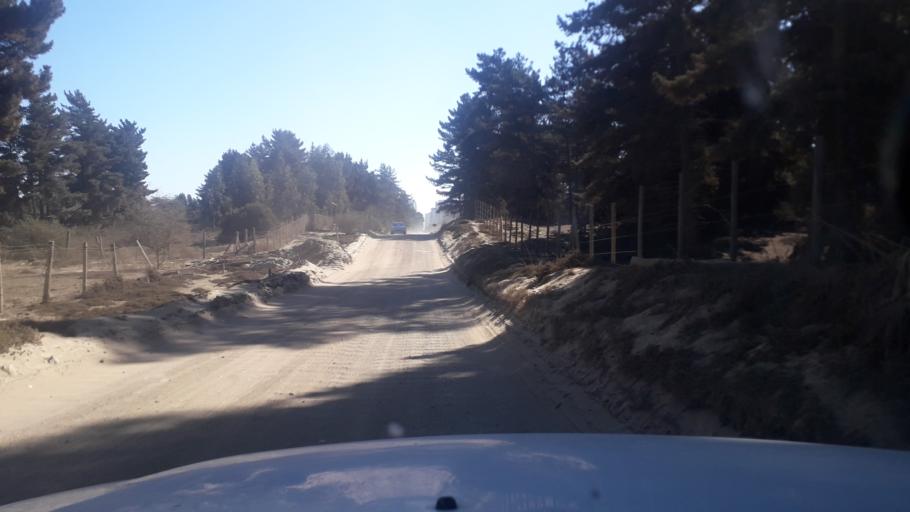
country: CL
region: Valparaiso
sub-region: Provincia de Valparaiso
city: Vina del Mar
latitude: -32.9536
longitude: -71.5302
